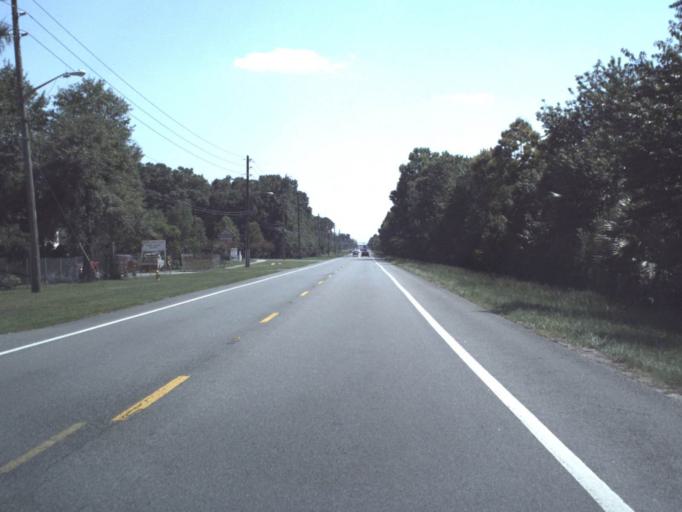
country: US
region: Florida
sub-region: Nassau County
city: Yulee
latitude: 30.4830
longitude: -81.6275
